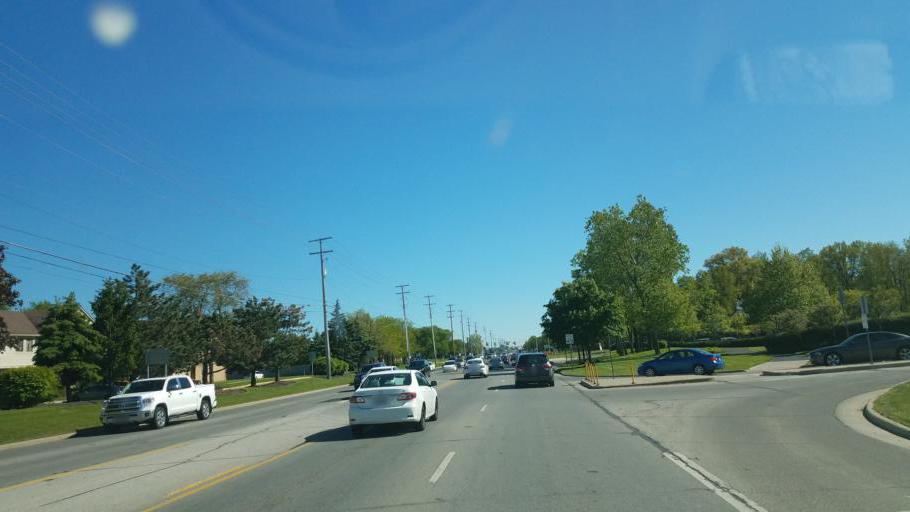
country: US
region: Ohio
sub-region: Franklin County
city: Dublin
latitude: 40.1211
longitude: -83.0903
